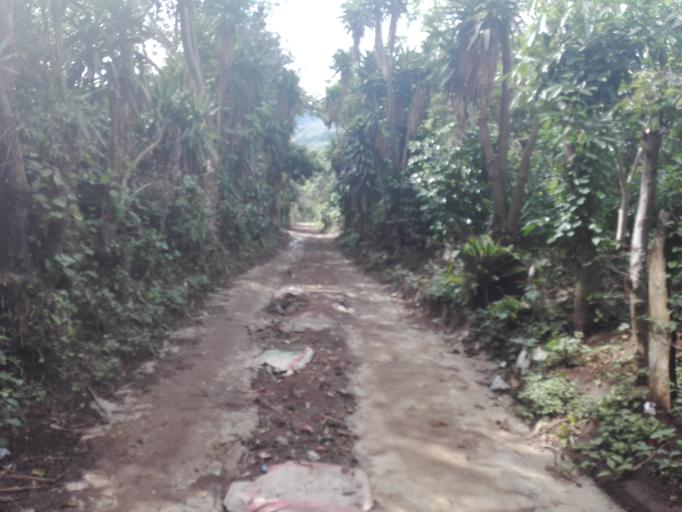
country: GT
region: Escuintla
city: San Vicente Pacaya
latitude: 14.3707
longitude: -90.5605
